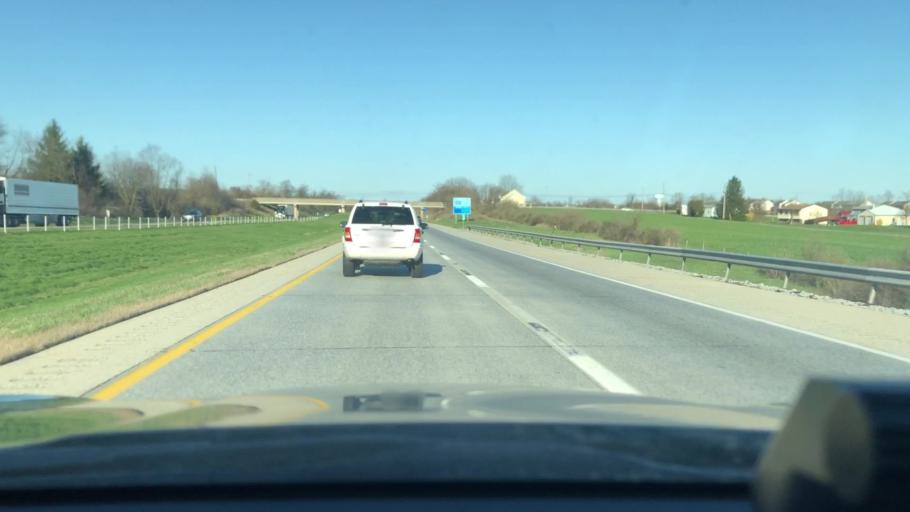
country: US
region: Pennsylvania
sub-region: Lebanon County
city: Fredericksburg
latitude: 40.4513
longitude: -76.4370
